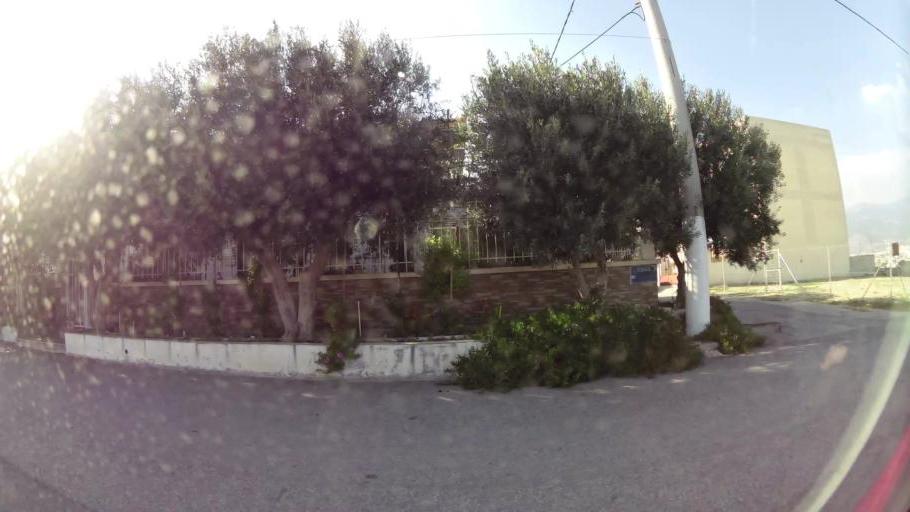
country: GR
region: Attica
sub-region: Nomarchia Dytikis Attikis
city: Zefyri
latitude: 38.0701
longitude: 23.7298
